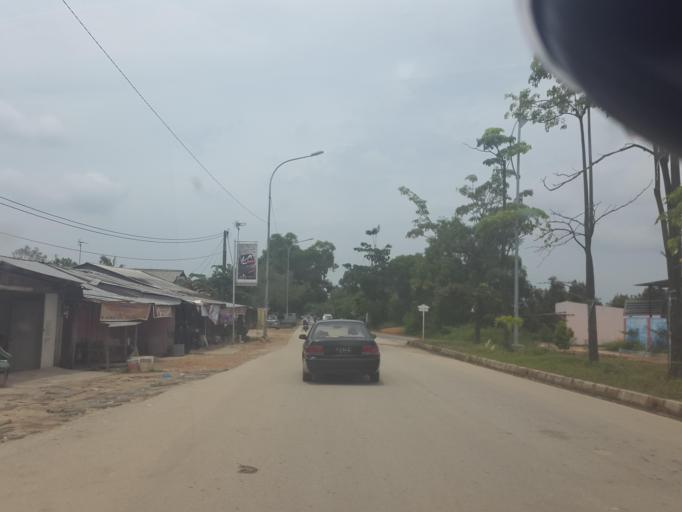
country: SG
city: Singapore
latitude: 1.1491
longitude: 104.1324
